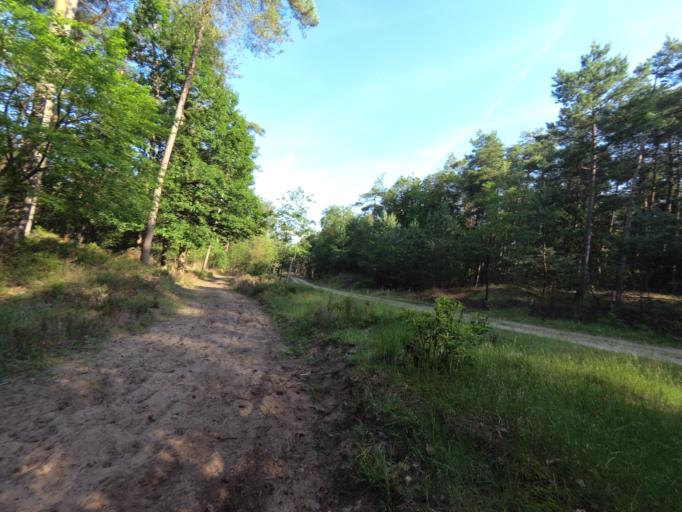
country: NL
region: Gelderland
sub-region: Gemeente Apeldoorn
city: Beekbergen
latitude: 52.1613
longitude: 5.8781
